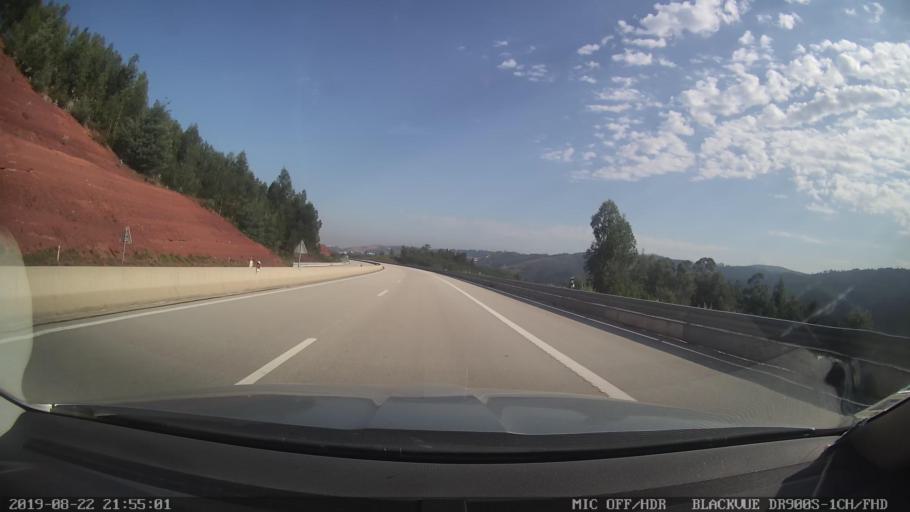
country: PT
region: Coimbra
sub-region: Coimbra
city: Coimbra
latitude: 40.1457
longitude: -8.3830
